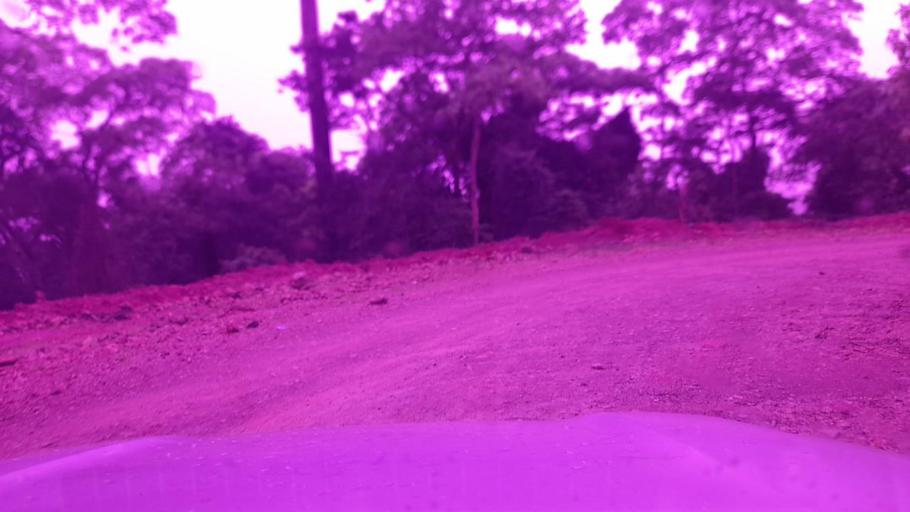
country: ET
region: Southern Nations, Nationalities, and People's Region
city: Bonga
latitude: 7.5129
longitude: 36.0563
